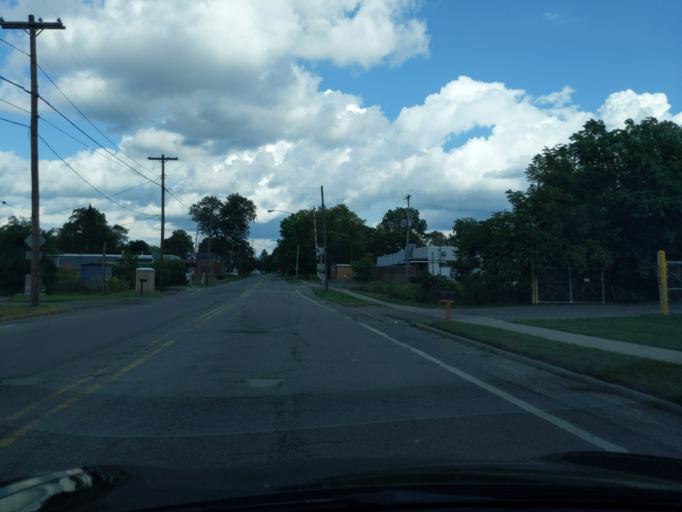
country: US
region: Michigan
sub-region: Jackson County
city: Jackson
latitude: 42.2651
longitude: -84.4085
